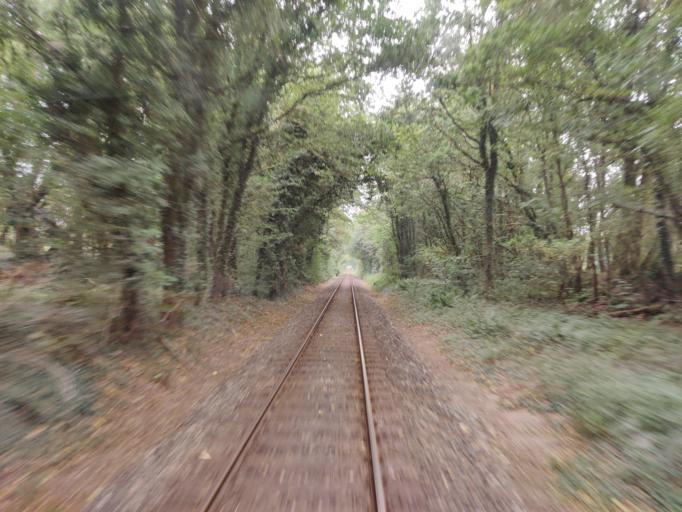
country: DE
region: Lower Saxony
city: Deinste
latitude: 53.5245
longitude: 9.4348
